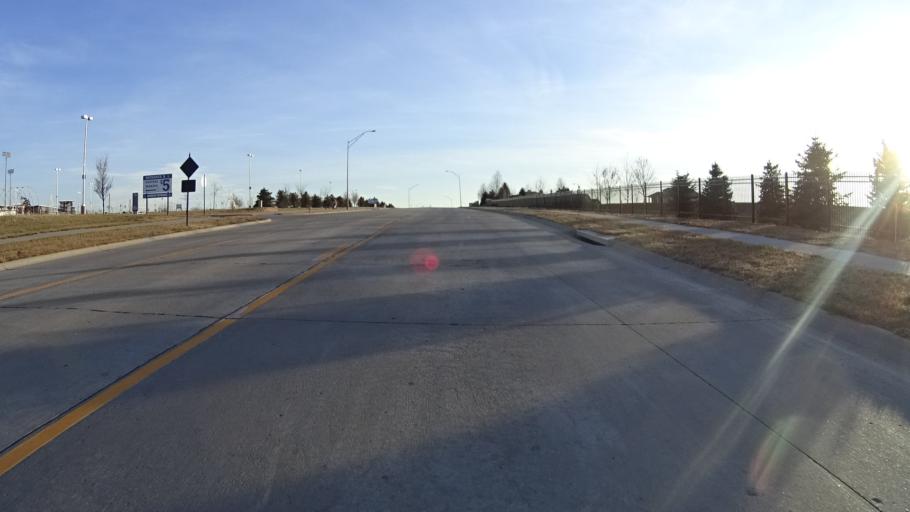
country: US
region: Nebraska
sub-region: Sarpy County
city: Chalco
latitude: 41.1536
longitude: -96.1099
